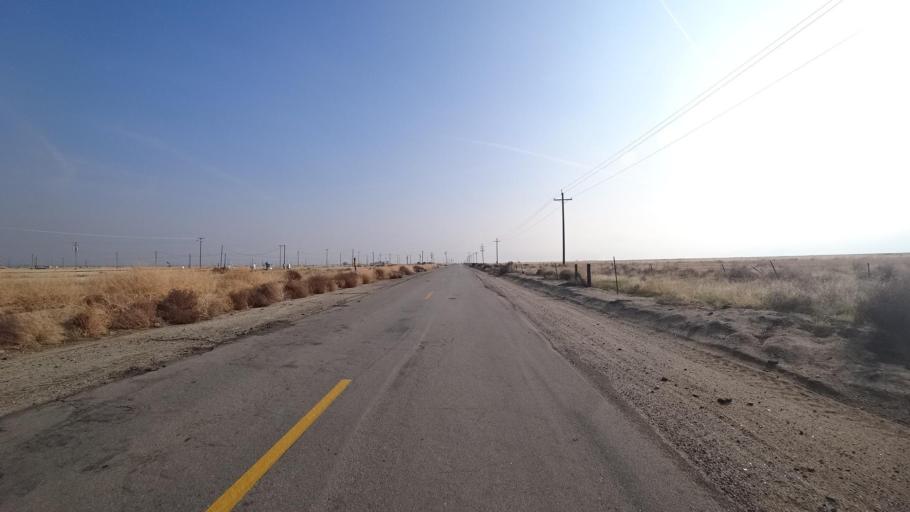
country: US
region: California
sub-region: Kern County
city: Lebec
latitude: 34.9845
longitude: -118.9279
